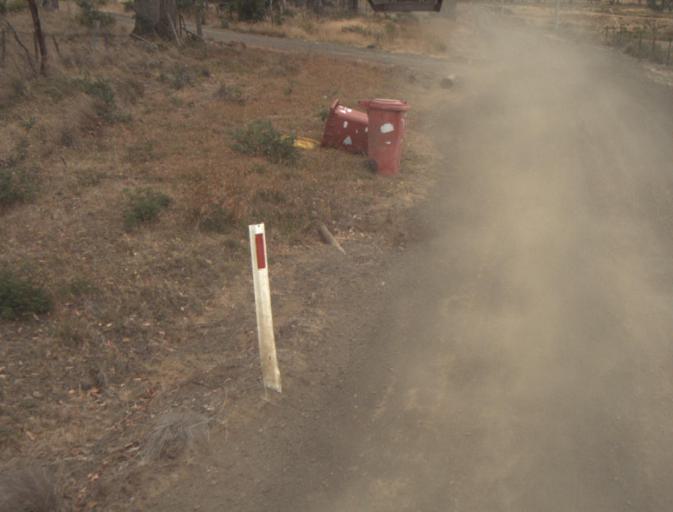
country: AU
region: Tasmania
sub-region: Northern Midlands
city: Evandale
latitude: -41.5208
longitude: 147.4444
